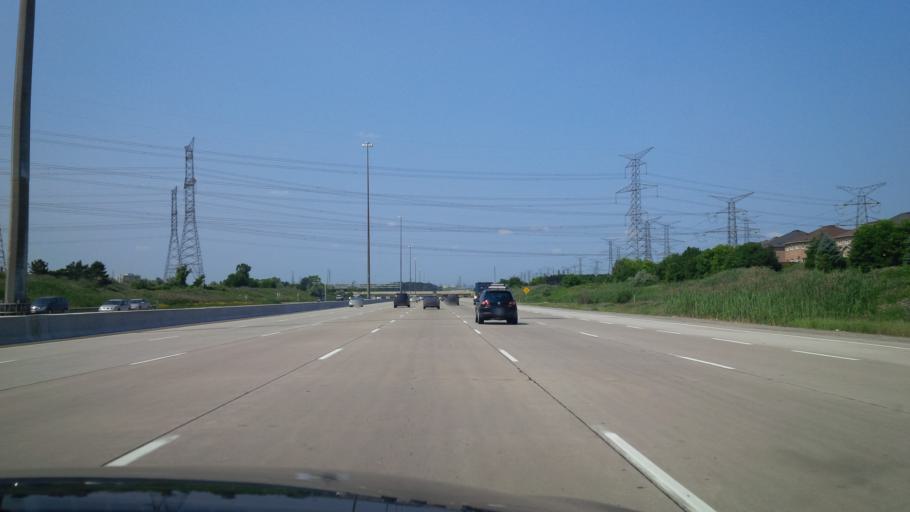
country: CA
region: Ontario
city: Concord
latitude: 43.7739
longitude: -79.5713
